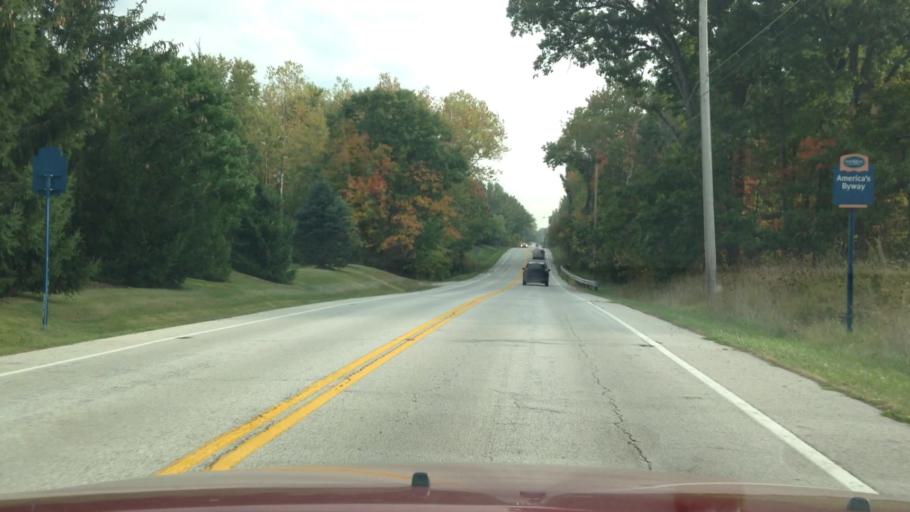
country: US
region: Ohio
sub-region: Cuyahoga County
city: Walton Hills
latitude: 41.3384
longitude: -81.5783
